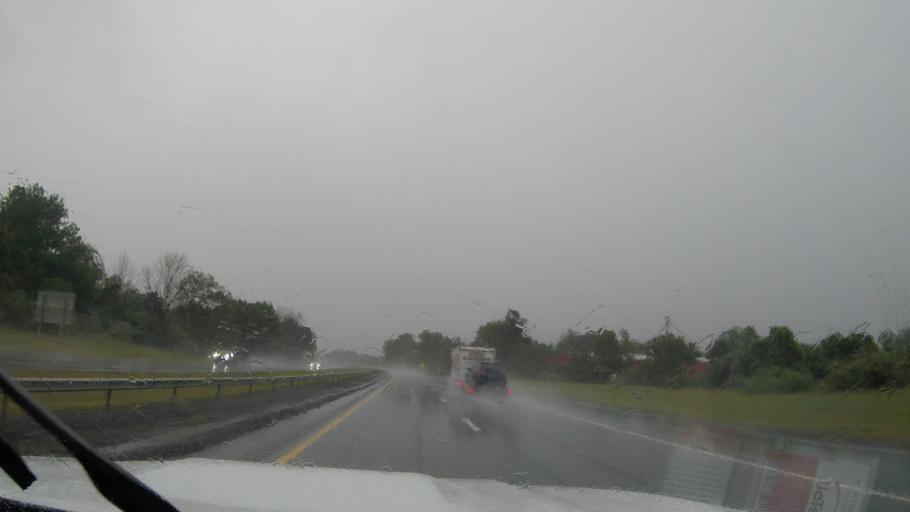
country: US
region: New York
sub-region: Ontario County
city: Geneva
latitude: 42.9547
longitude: -76.9704
